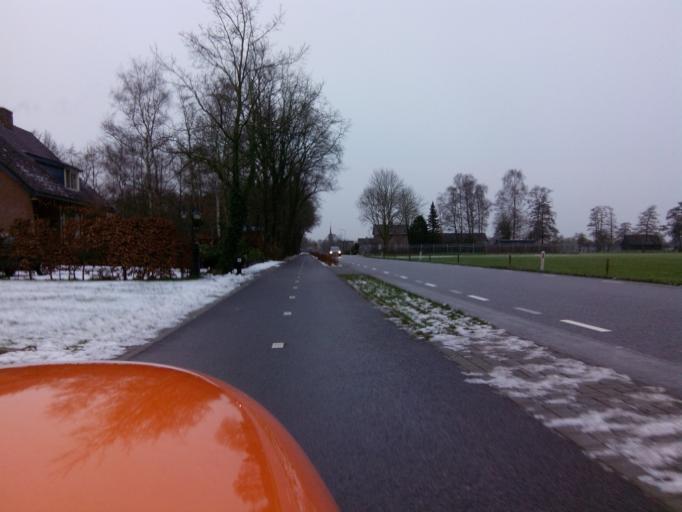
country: NL
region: Gelderland
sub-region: Gemeente Barneveld
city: Terschuur
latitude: 52.1698
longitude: 5.5156
